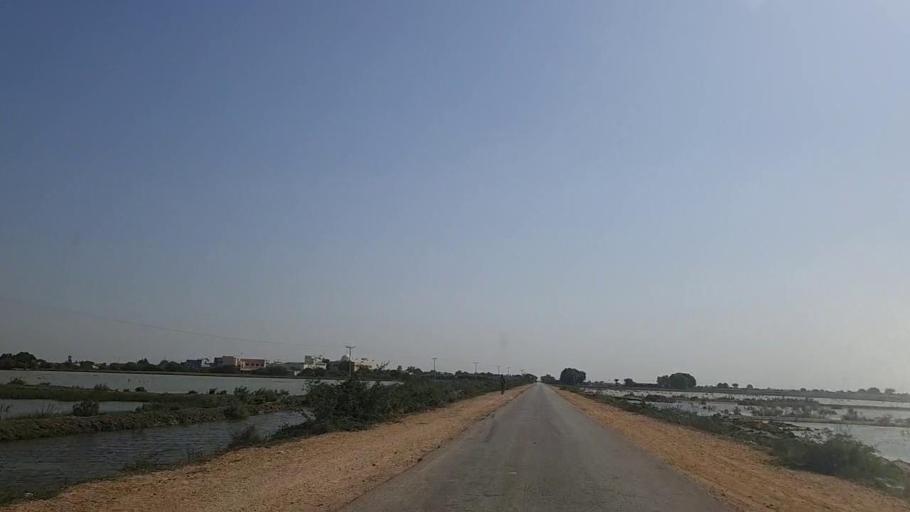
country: PK
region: Sindh
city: Mirpur Batoro
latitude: 24.6446
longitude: 68.2899
